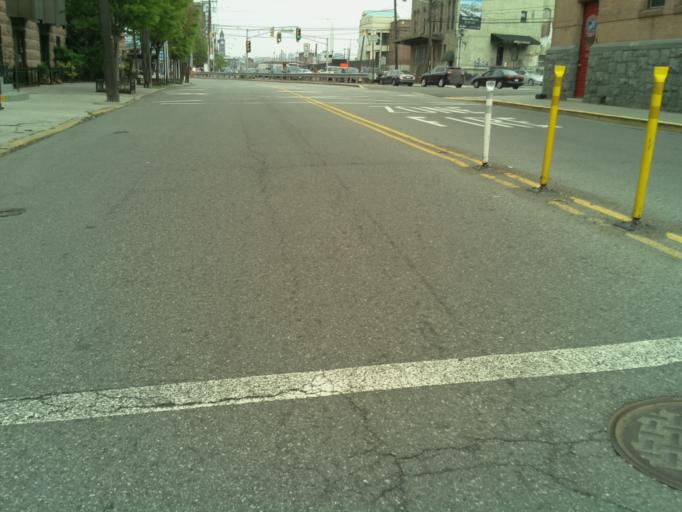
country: US
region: New Jersey
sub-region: Hudson County
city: Hoboken
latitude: 40.7371
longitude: -74.0396
